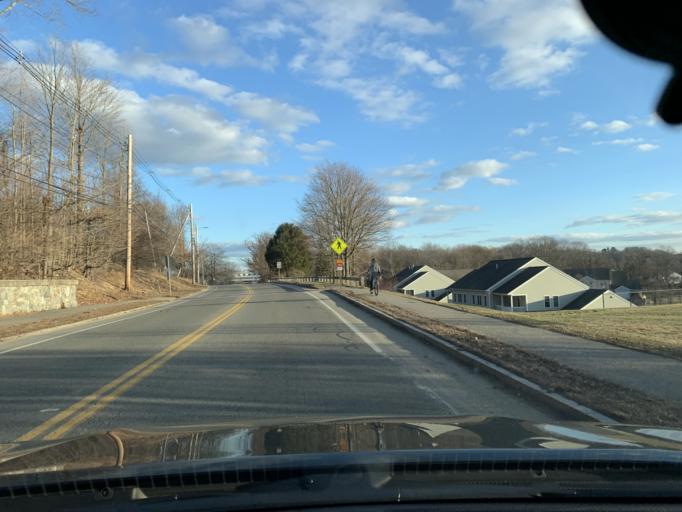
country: US
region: Massachusetts
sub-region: Essex County
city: Middleton
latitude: 42.5949
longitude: -70.9852
